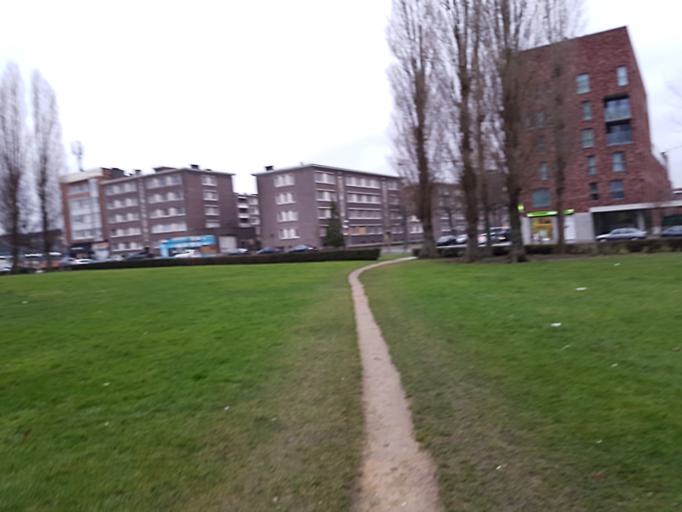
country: BE
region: Flanders
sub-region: Provincie Antwerpen
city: Antwerpen
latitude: 51.2541
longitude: 4.4221
